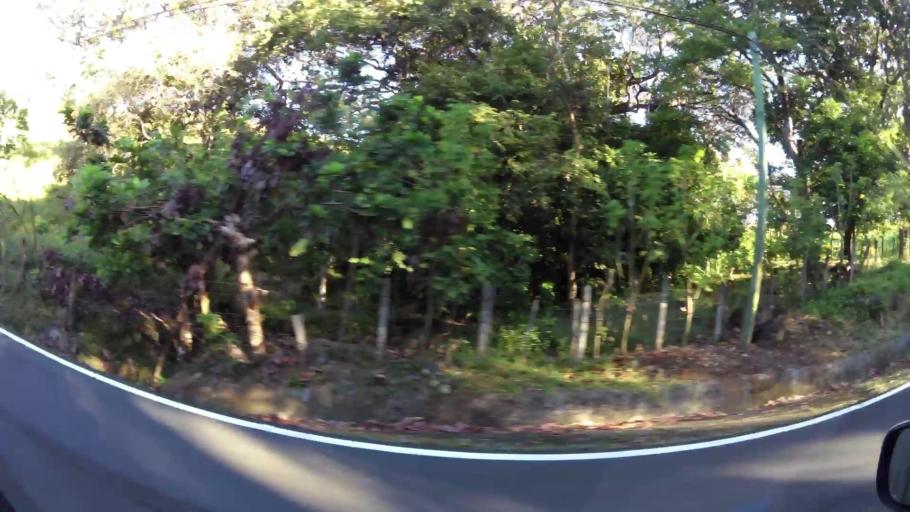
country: CR
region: Puntarenas
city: Miramar
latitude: 10.1649
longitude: -84.8532
